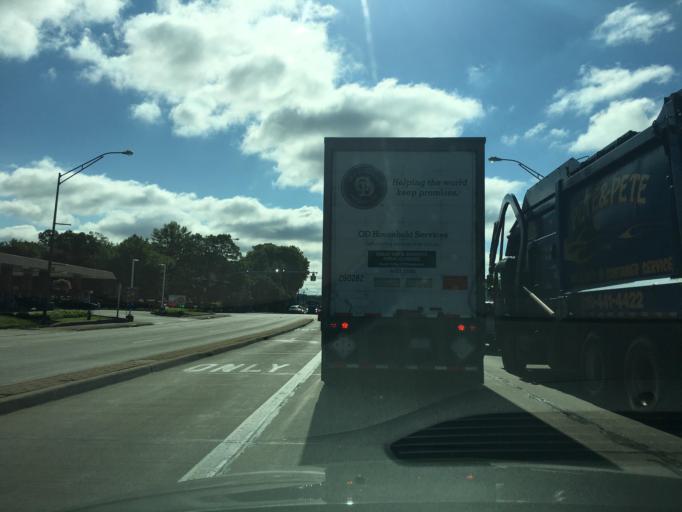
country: US
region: Ohio
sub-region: Cuyahoga County
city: Independence
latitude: 41.3944
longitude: -81.6421
